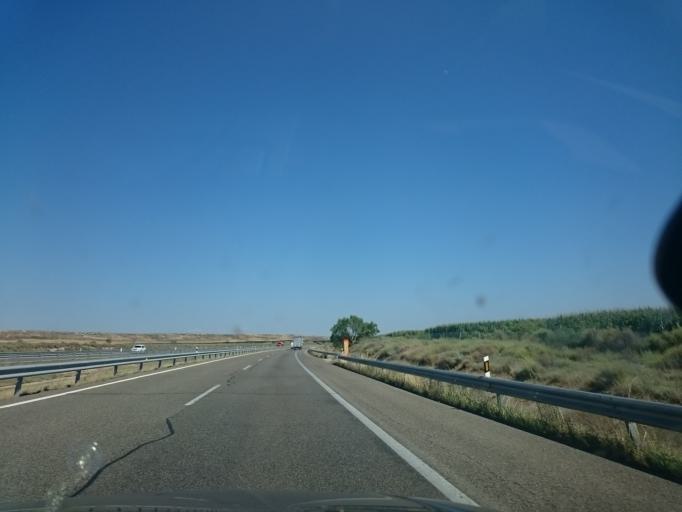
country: ES
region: Aragon
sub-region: Provincia de Huesca
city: Candasnos
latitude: 41.5236
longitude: 0.0709
